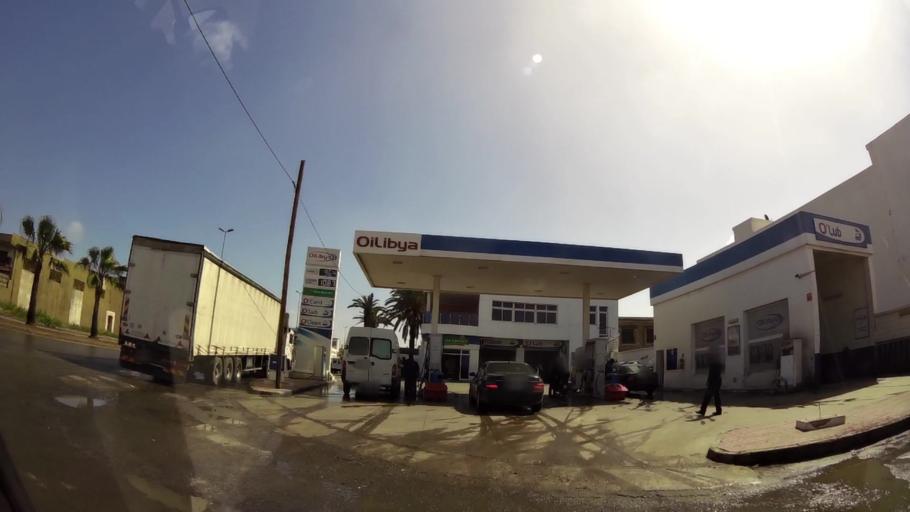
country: MA
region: Grand Casablanca
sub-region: Mediouna
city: Tit Mellil
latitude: 33.6210
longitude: -7.5117
